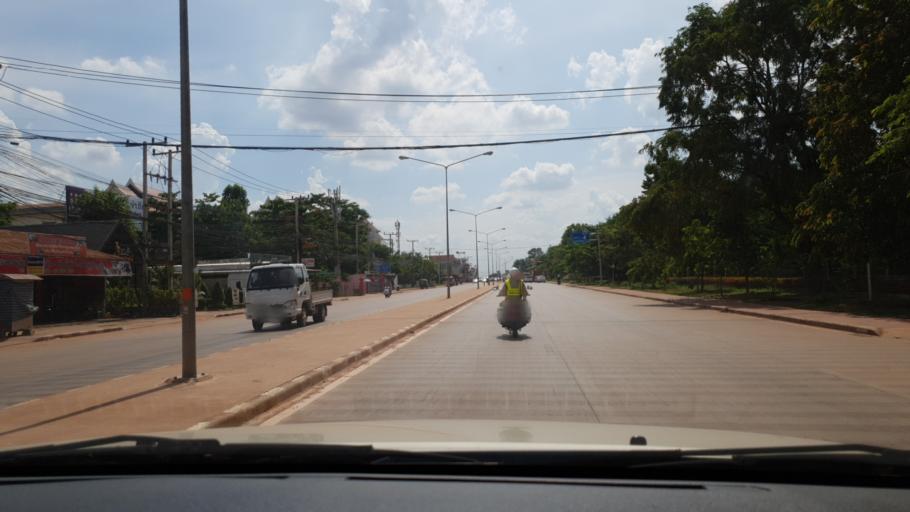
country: LA
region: Vientiane
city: Vientiane
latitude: 18.0335
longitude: 102.6370
